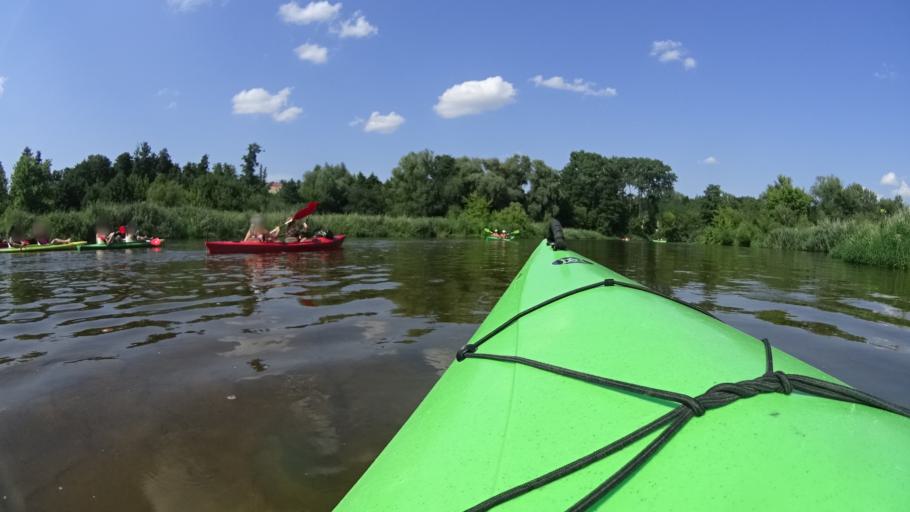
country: PL
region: Masovian Voivodeship
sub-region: Powiat bialobrzeski
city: Bialobrzegi
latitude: 51.6646
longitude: 20.8858
